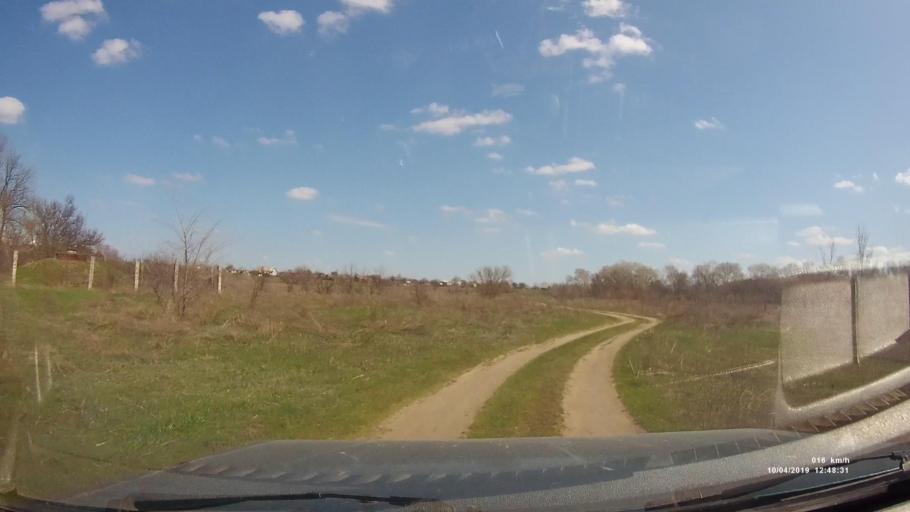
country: RU
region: Rostov
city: Kamensk-Shakhtinskiy
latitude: 48.3558
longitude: 40.2227
